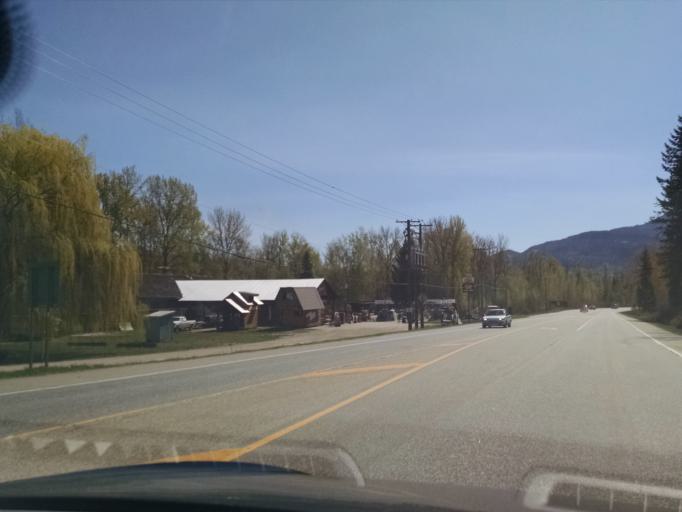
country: CA
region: British Columbia
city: Salmon Arm
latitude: 50.7342
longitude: -119.3181
